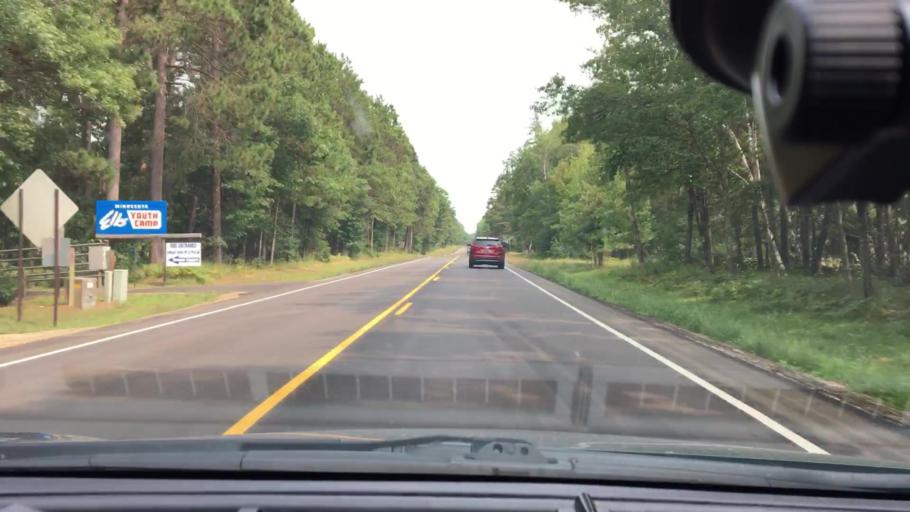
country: US
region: Minnesota
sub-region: Crow Wing County
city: Breezy Point
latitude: 46.5335
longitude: -94.1804
